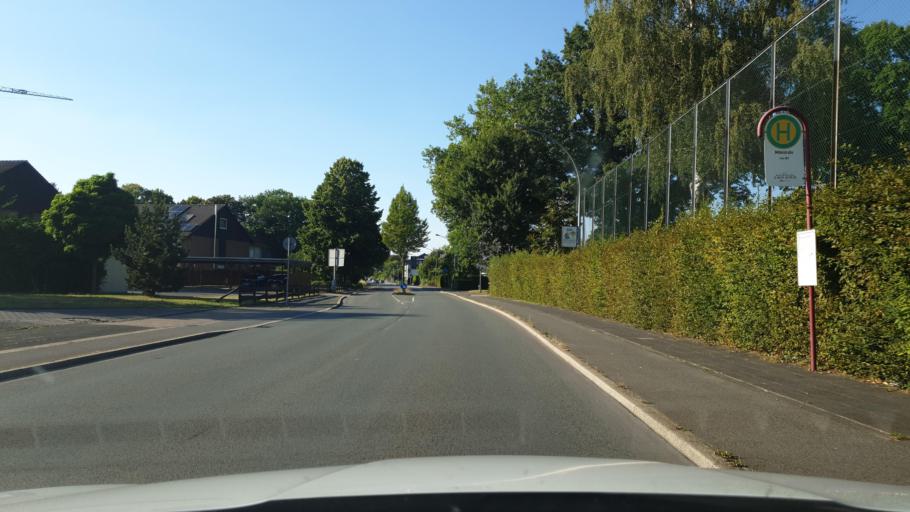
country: DE
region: North Rhine-Westphalia
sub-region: Regierungsbezirk Detmold
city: Bad Salzuflen
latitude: 52.0669
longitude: 8.7687
